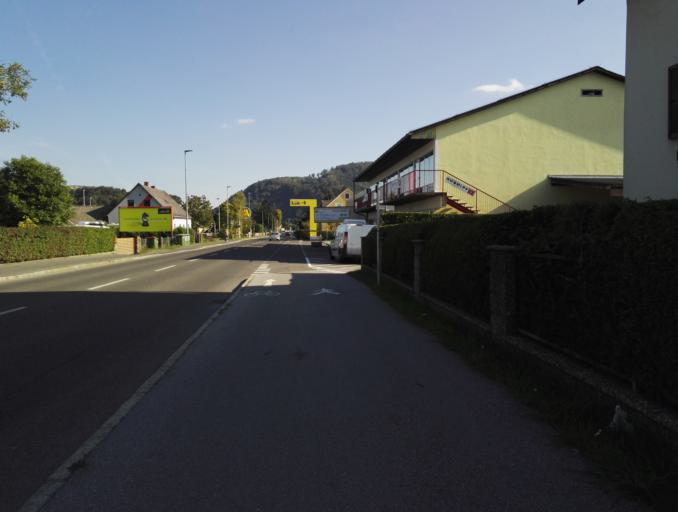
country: AT
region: Styria
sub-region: Politischer Bezirk Graz-Umgebung
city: Gratkorn
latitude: 47.1285
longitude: 15.3449
